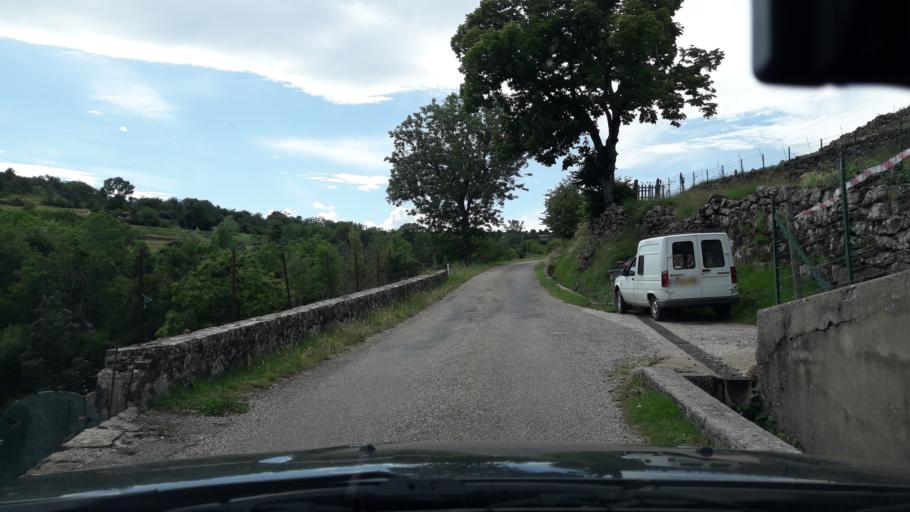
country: FR
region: Rhone-Alpes
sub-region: Departement de l'Ardeche
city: Saint-Priest
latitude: 44.6825
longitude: 4.5716
